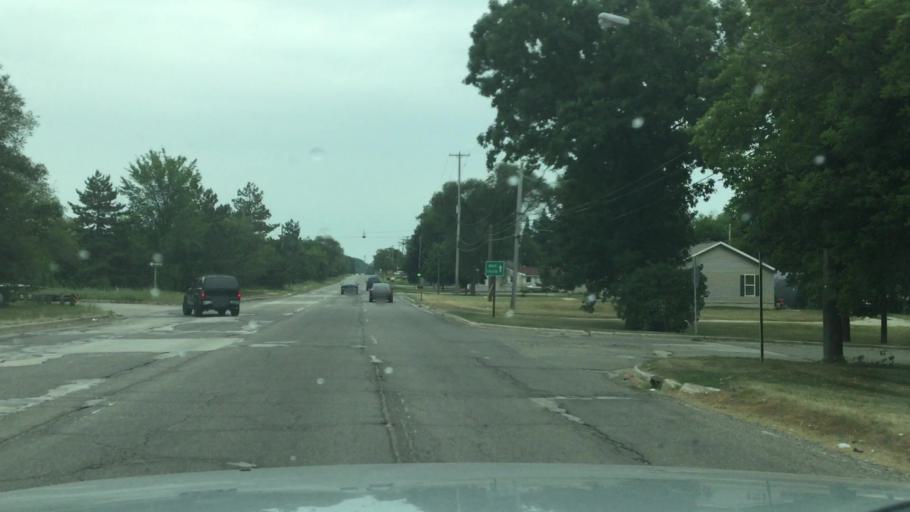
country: US
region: Michigan
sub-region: Genesee County
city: Flint
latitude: 42.9809
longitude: -83.6830
